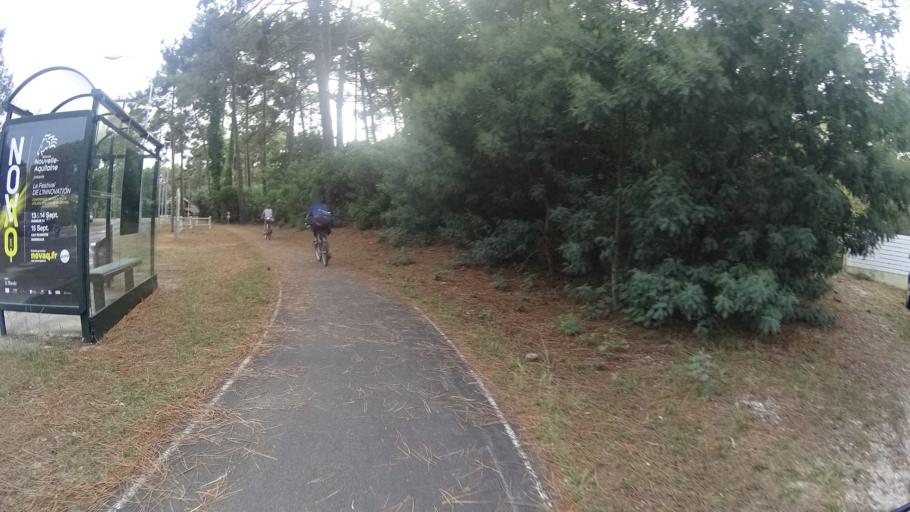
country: FR
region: Aquitaine
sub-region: Departement de la Gironde
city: Lacanau
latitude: 44.9934
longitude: -1.1464
